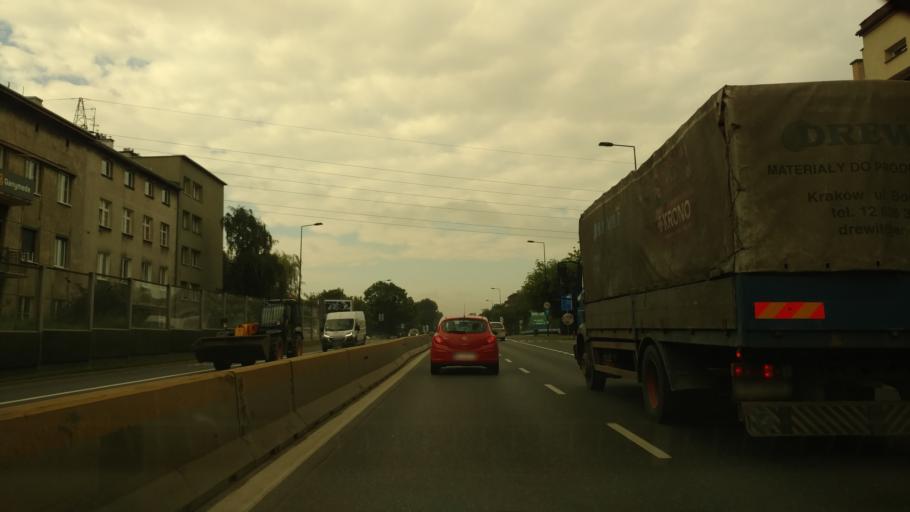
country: PL
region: Lesser Poland Voivodeship
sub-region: Krakow
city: Krakow
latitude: 50.0814
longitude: 19.9512
